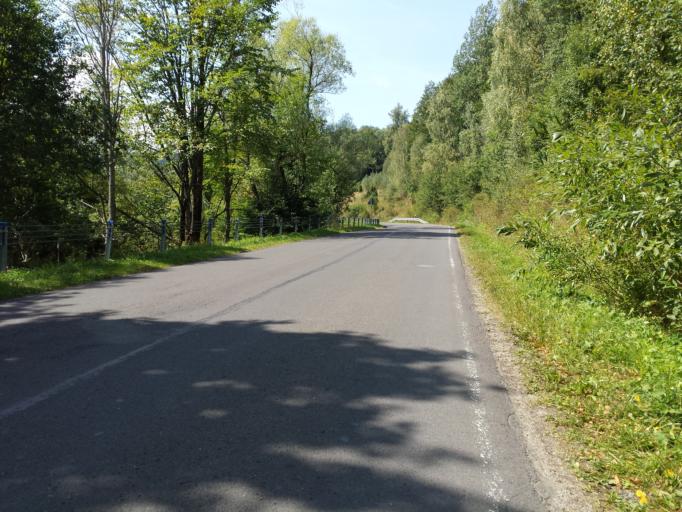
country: PL
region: Subcarpathian Voivodeship
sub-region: Powiat bieszczadzki
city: Lutowiska
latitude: 49.1419
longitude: 22.5660
